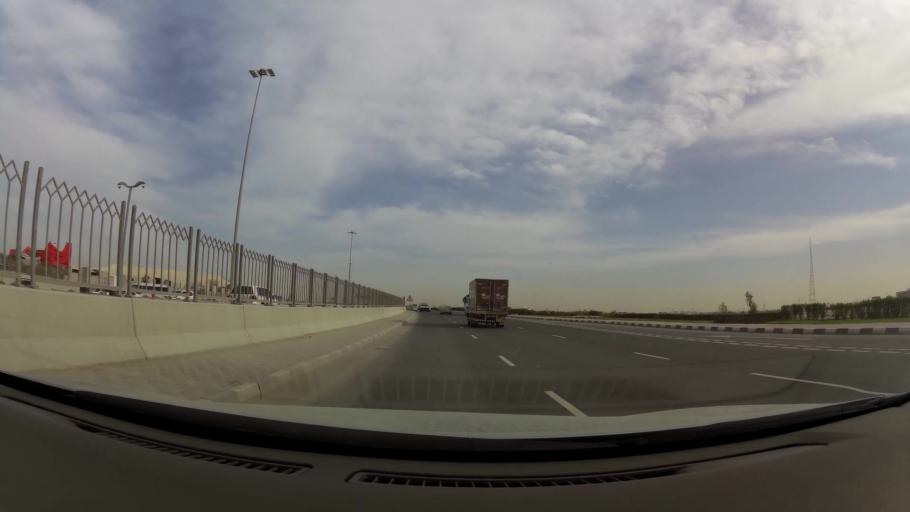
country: QA
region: Baladiyat ad Dawhah
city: Doha
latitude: 25.2925
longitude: 51.4759
